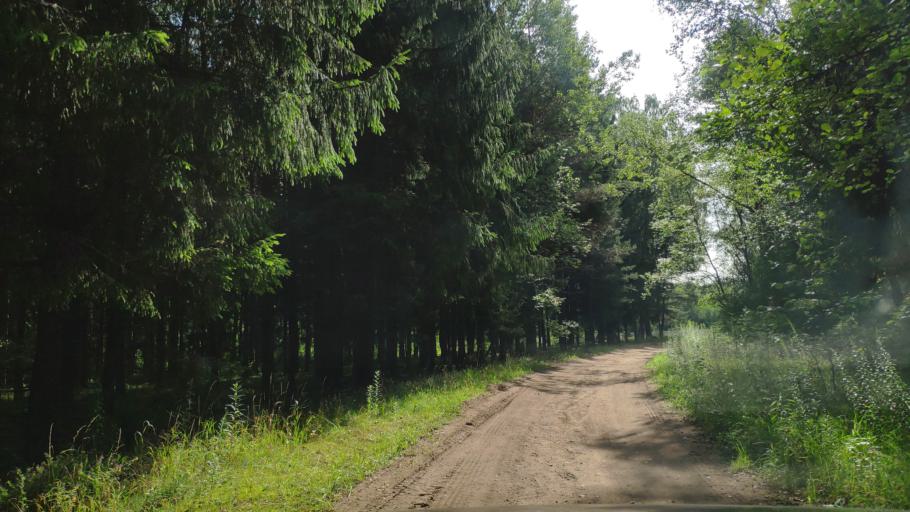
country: BY
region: Minsk
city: Zaslawye
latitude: 53.9737
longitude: 27.2921
